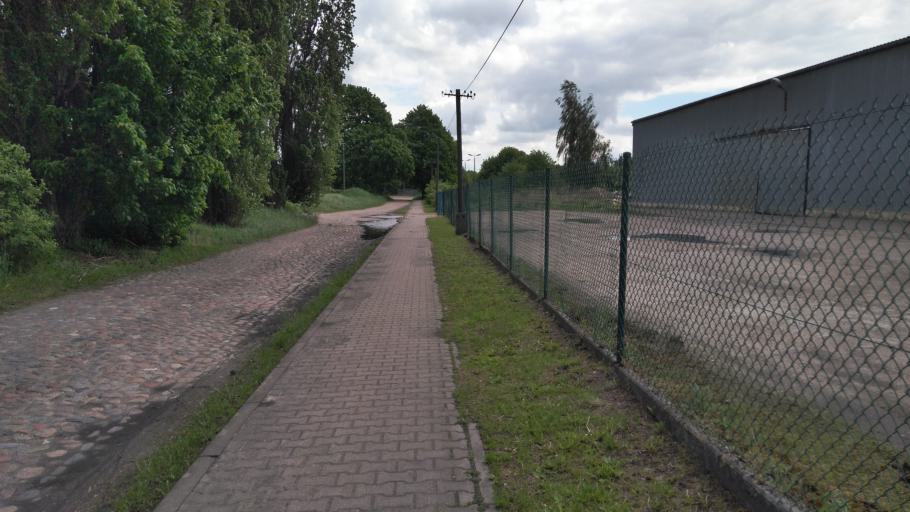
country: PL
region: Kujawsko-Pomorskie
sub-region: Powiat grudziadzki
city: Gruta
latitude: 53.4372
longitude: 18.9447
